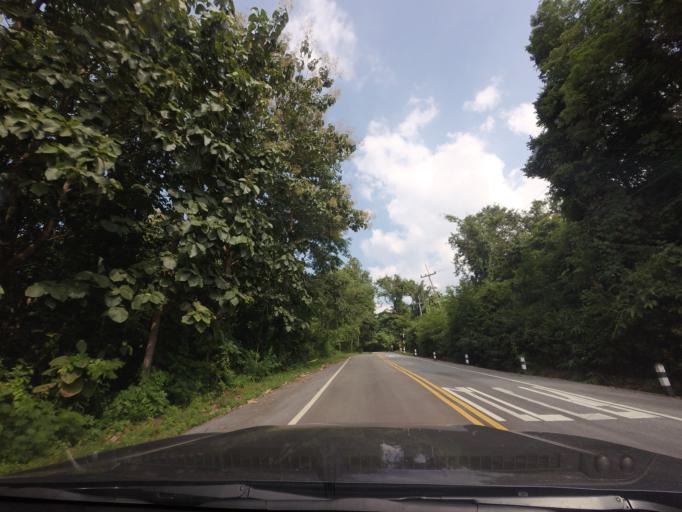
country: TH
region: Phitsanulok
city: Nakhon Thai
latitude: 17.0225
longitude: 100.9387
